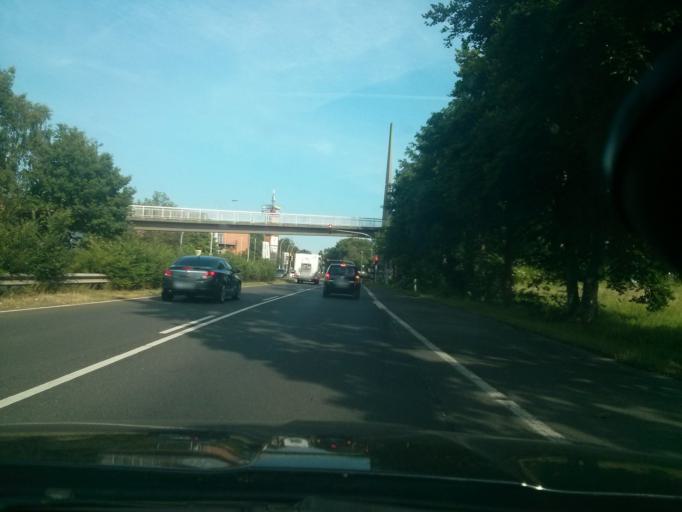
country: DE
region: Schleswig-Holstein
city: Halstenbek
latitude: 53.6015
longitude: 9.8350
